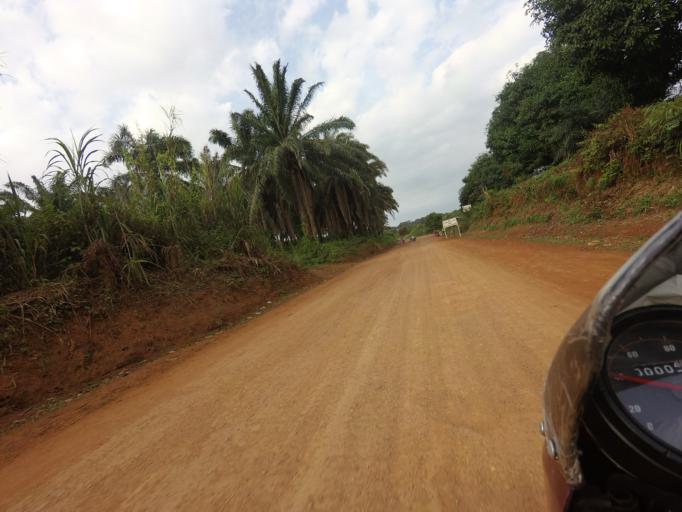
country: SL
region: Eastern Province
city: Kailahun
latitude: 8.2631
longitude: -10.5835
